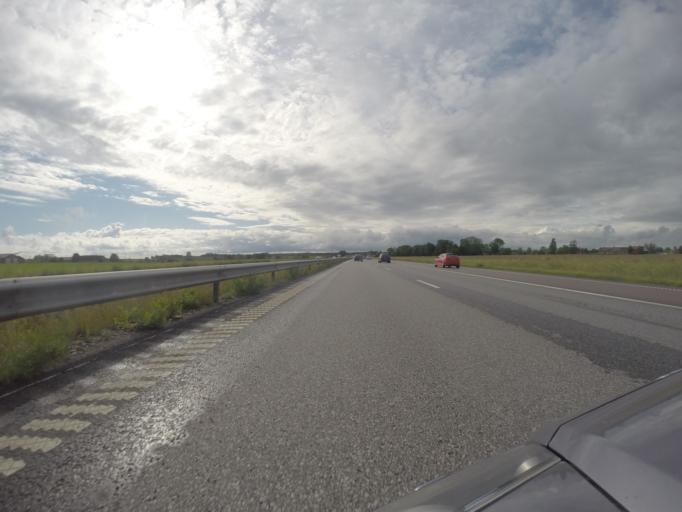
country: SE
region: Skane
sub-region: Kavlinge Kommun
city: Loddekopinge
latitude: 55.7472
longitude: 13.0224
